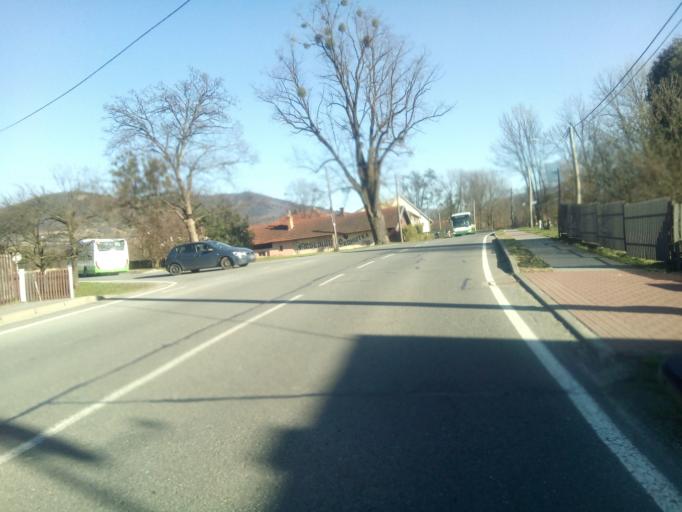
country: CZ
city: Raskovice
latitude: 49.6394
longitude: 18.4482
